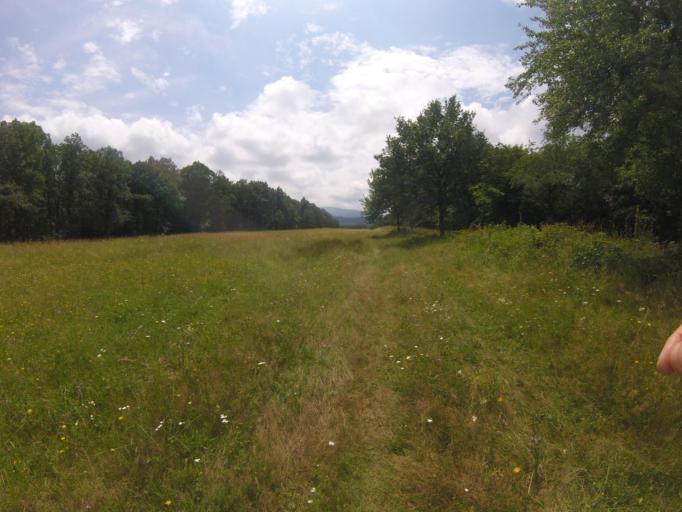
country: SK
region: Nitriansky
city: Sahy
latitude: 48.0206
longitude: 18.9623
